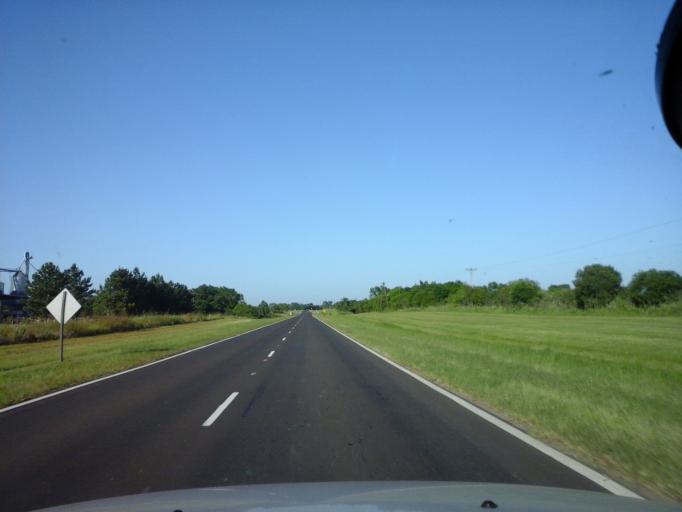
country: AR
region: Corrientes
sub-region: Departamento de Beron de Astrada
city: Beron de Astrada
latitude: -27.4662
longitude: -57.4701
